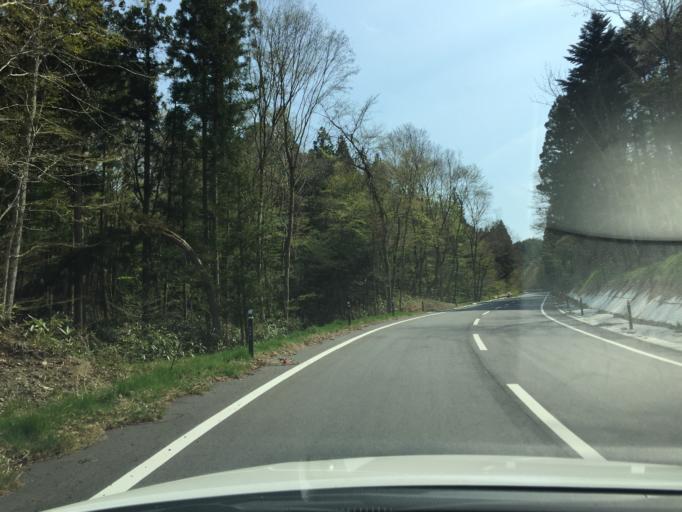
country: JP
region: Fukushima
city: Iwaki
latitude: 37.2493
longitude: 140.8488
